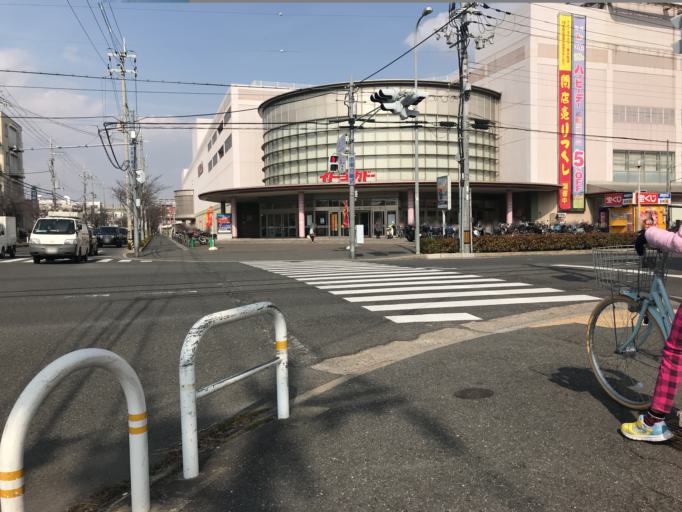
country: JP
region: Osaka
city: Daitocho
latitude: 34.6712
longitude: 135.6170
